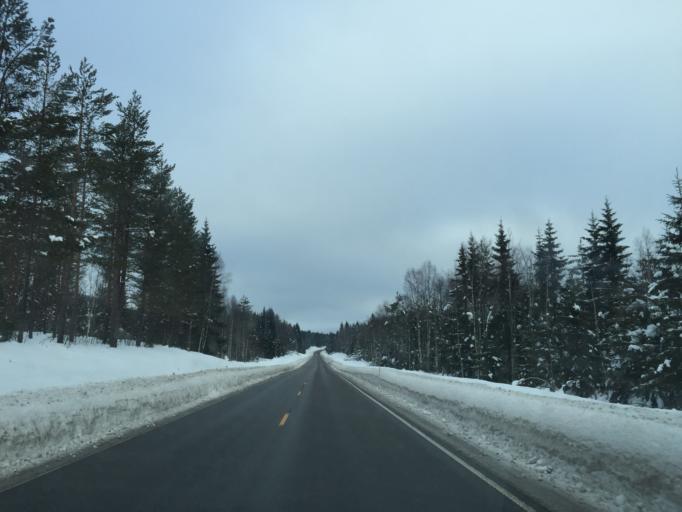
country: NO
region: Hedmark
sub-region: Trysil
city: Innbygda
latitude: 61.1650
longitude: 12.1511
